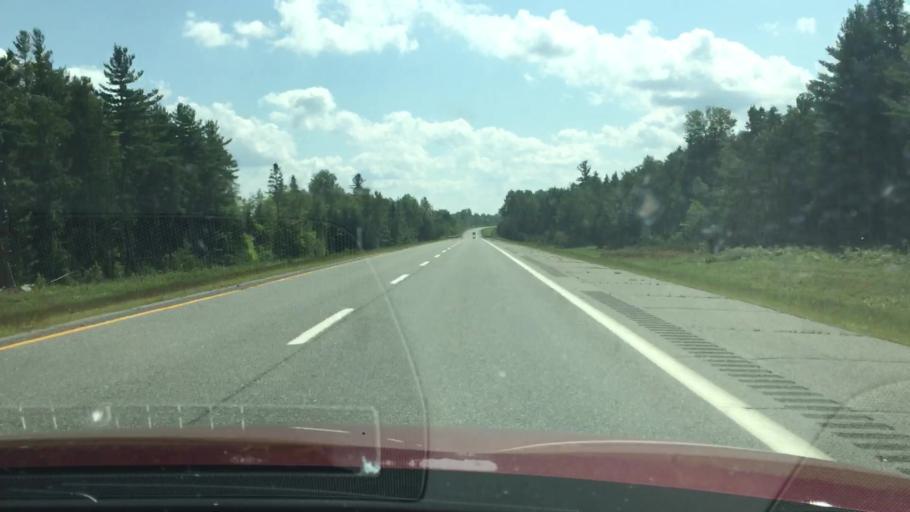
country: US
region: Maine
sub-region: Penobscot County
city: Lincoln
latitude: 45.4383
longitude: -68.5903
